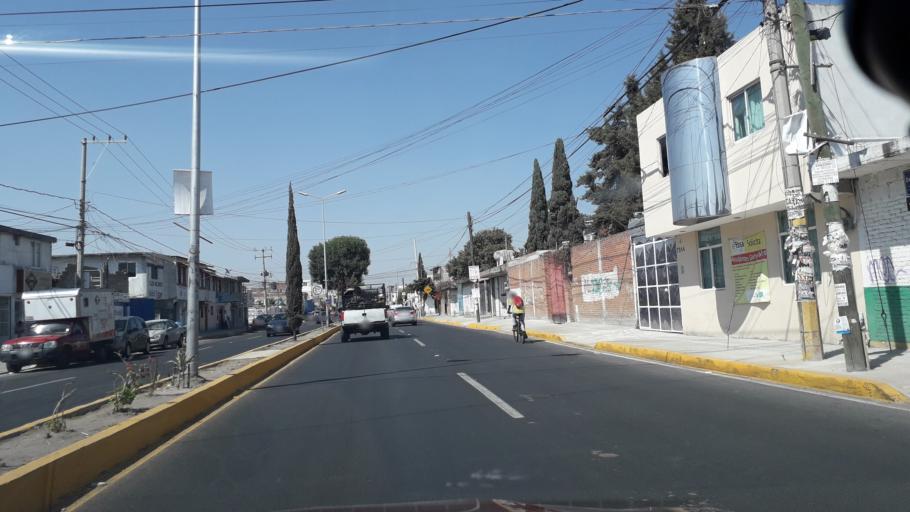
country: MX
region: Puebla
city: Puebla
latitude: 18.9958
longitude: -98.2114
